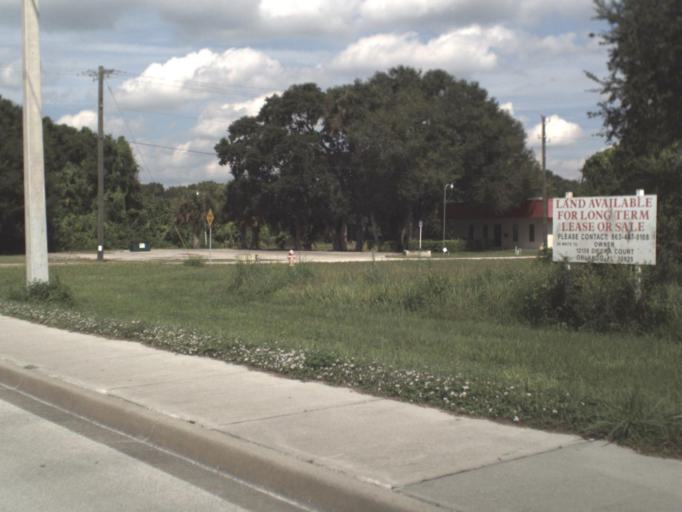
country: US
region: Florida
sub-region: Okeechobee County
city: Okeechobee
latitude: 27.2566
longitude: -80.8299
